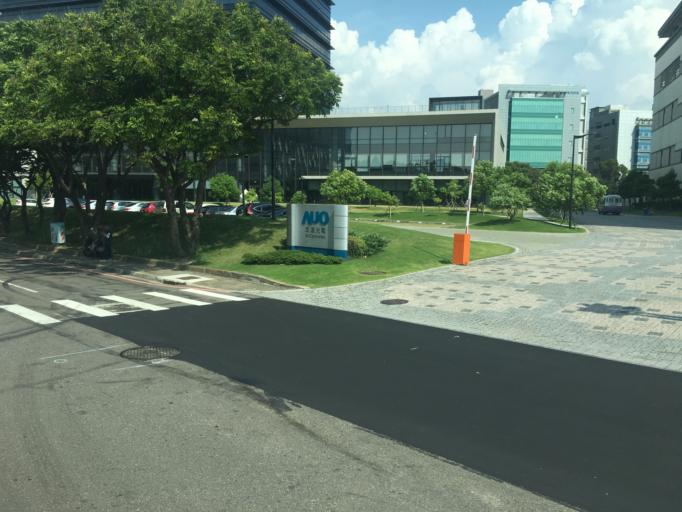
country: TW
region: Taiwan
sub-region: Hsinchu
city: Hsinchu
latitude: 24.7768
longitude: 121.0070
